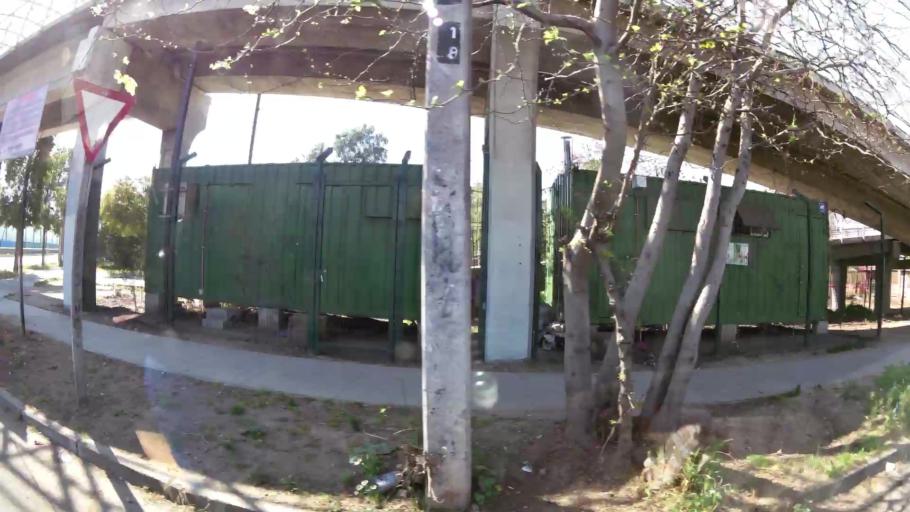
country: CL
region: Santiago Metropolitan
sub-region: Provincia de Santiago
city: Lo Prado
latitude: -33.4071
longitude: -70.6942
